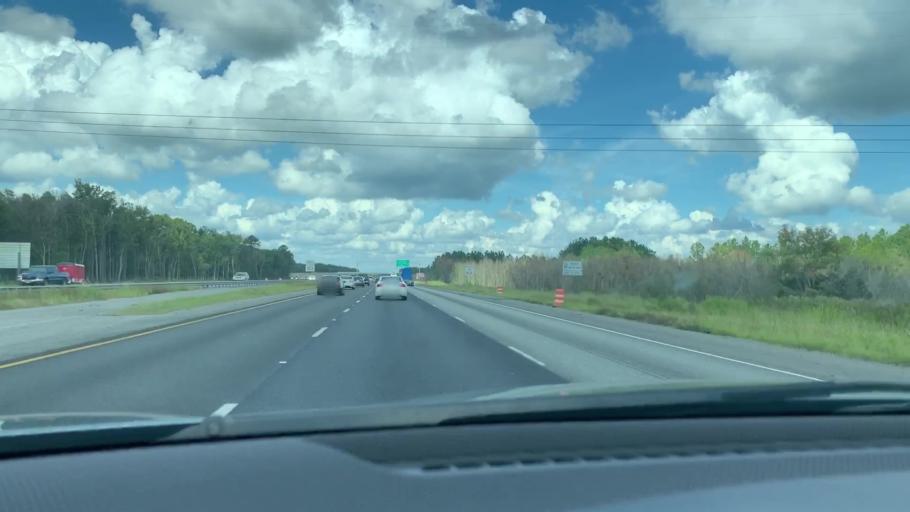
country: US
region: Georgia
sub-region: Camden County
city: Kingsland
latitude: 30.8173
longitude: -81.6646
